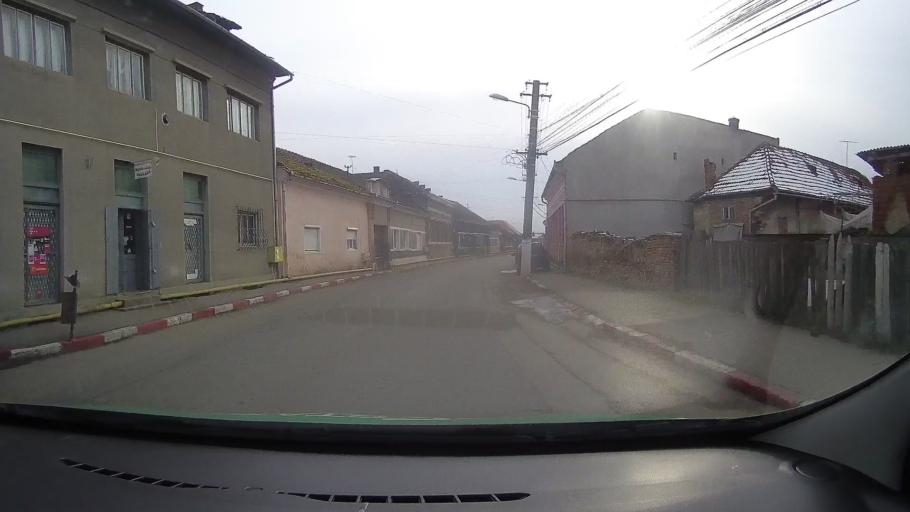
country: RO
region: Hunedoara
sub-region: Comuna Geoagiu
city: Geoagiu
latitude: 45.9240
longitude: 23.1995
